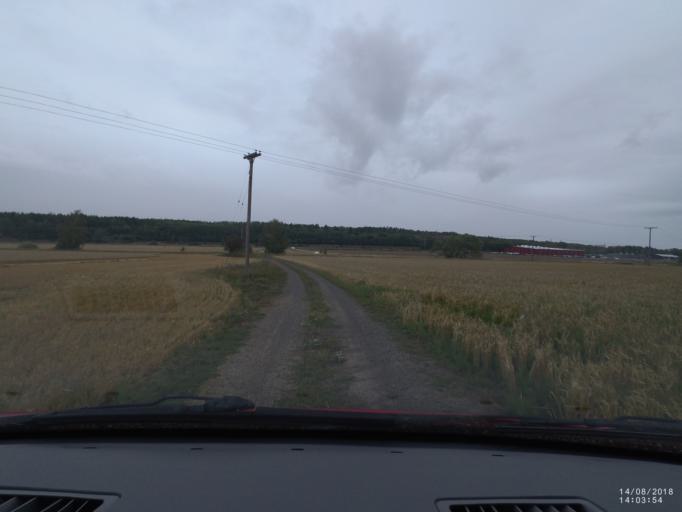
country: SE
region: Soedermanland
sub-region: Nykopings Kommun
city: Nykoping
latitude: 58.7540
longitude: 16.9615
